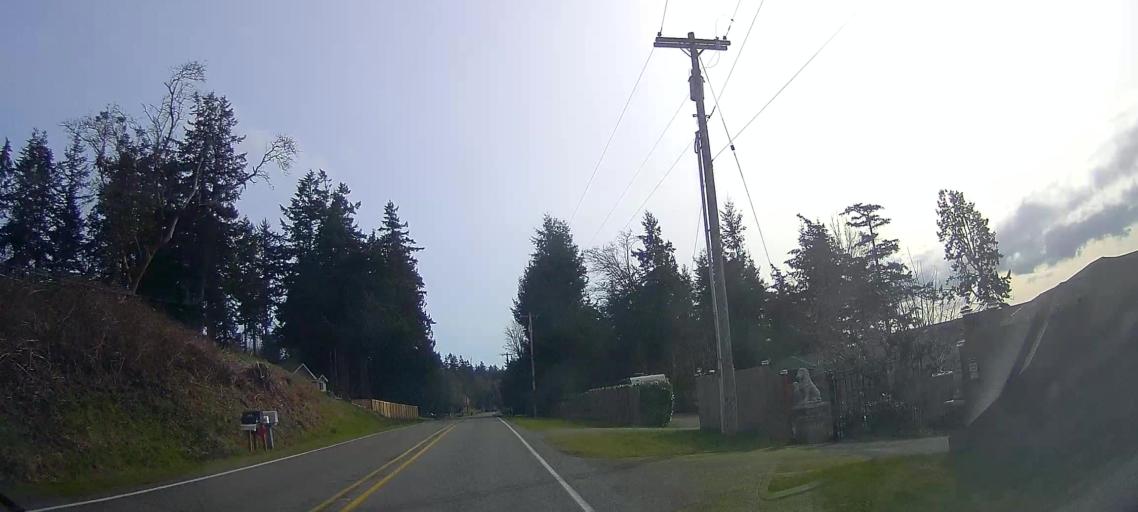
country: US
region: Washington
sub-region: Island County
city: Langley
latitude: 48.0825
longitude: -122.3948
